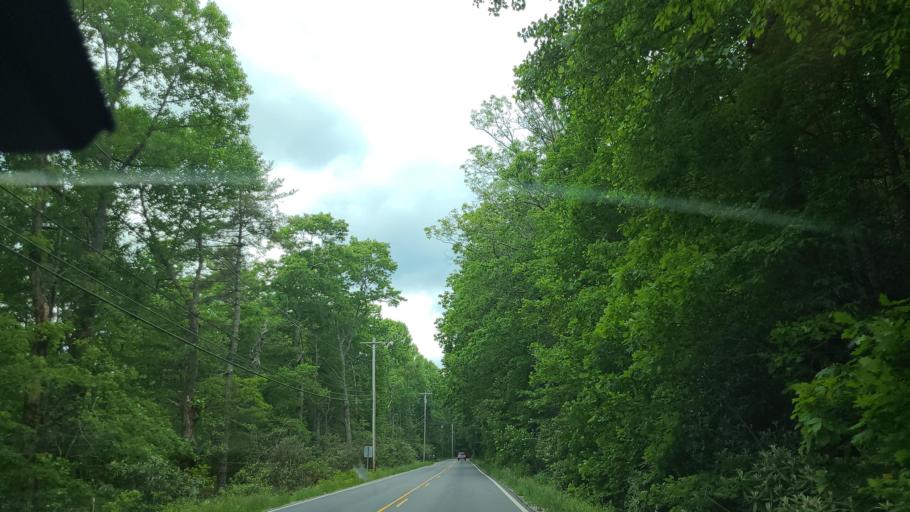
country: US
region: Georgia
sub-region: Rabun County
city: Mountain City
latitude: 35.0430
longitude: -83.2028
